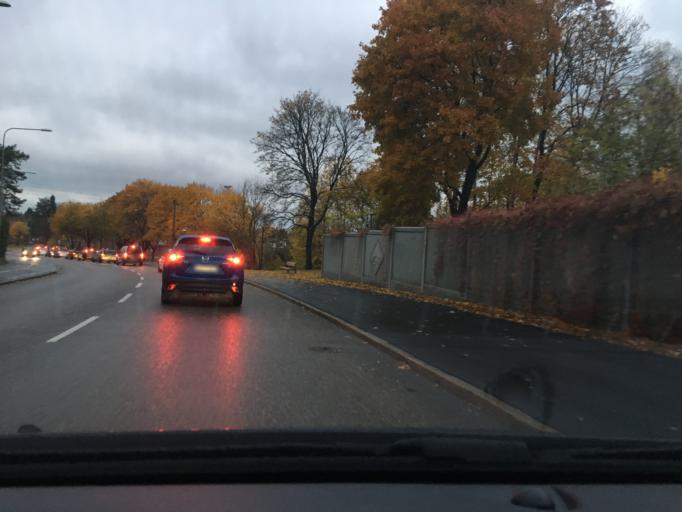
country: SE
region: Stockholm
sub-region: Stockholms Kommun
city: Kista
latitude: 59.3751
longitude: 17.9036
